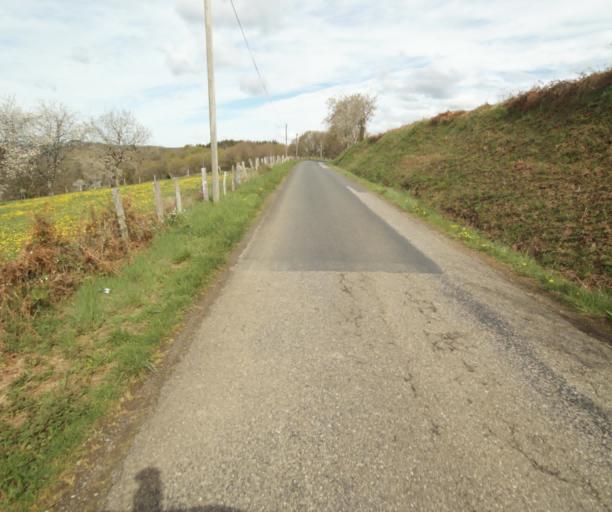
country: FR
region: Limousin
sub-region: Departement de la Correze
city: Laguenne
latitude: 45.2368
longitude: 1.8369
